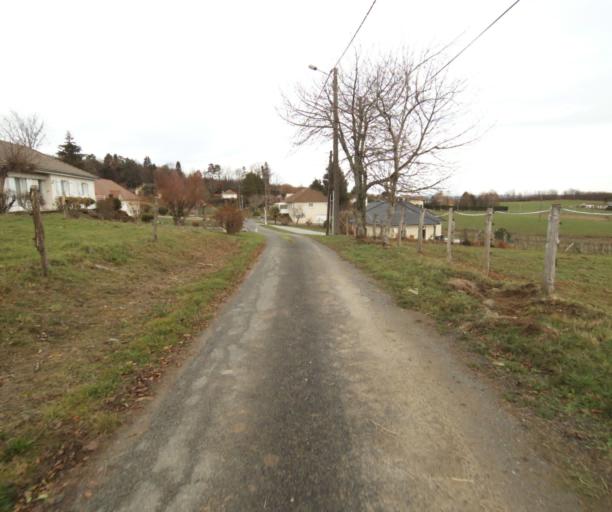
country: FR
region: Limousin
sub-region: Departement de la Correze
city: Chameyrat
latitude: 45.2664
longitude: 1.7009
